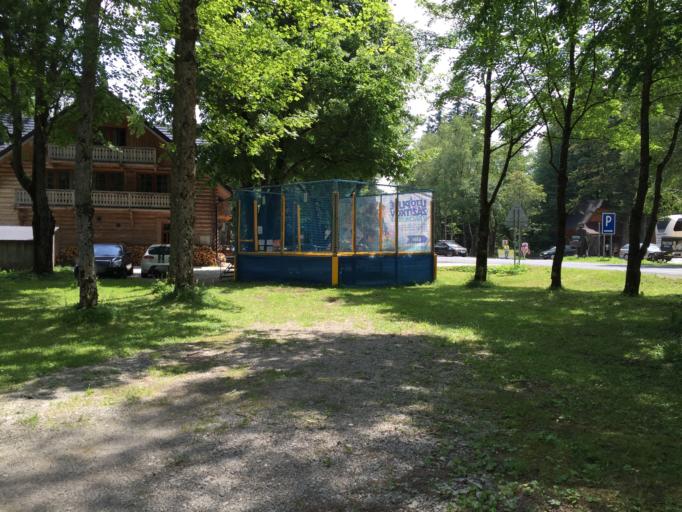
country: SK
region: Presovsky
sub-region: Okres Poprad
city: Zdiar
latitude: 49.2300
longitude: 20.3170
